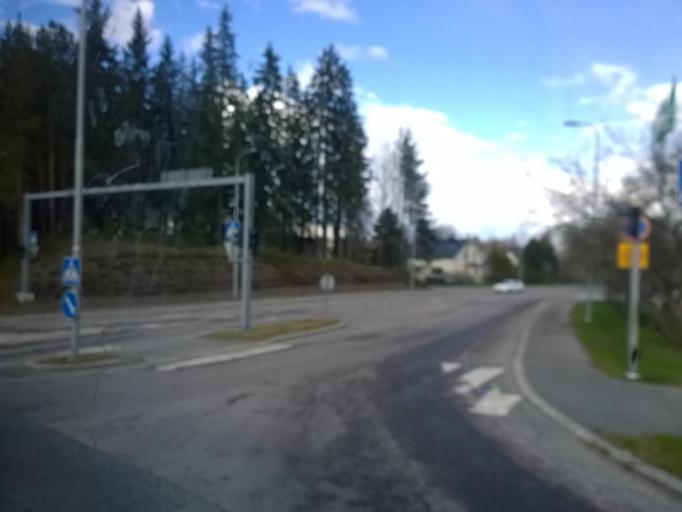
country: FI
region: Pirkanmaa
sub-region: Tampere
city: Tampere
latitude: 61.4694
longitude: 23.7749
